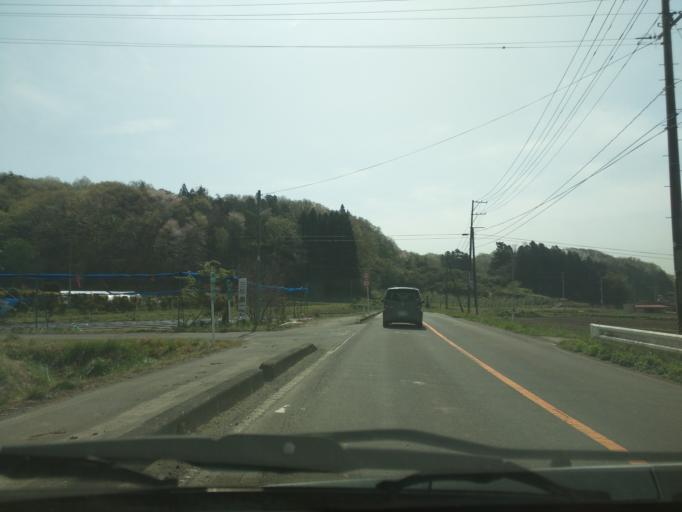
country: JP
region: Fukushima
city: Nihommatsu
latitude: 37.5960
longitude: 140.4059
